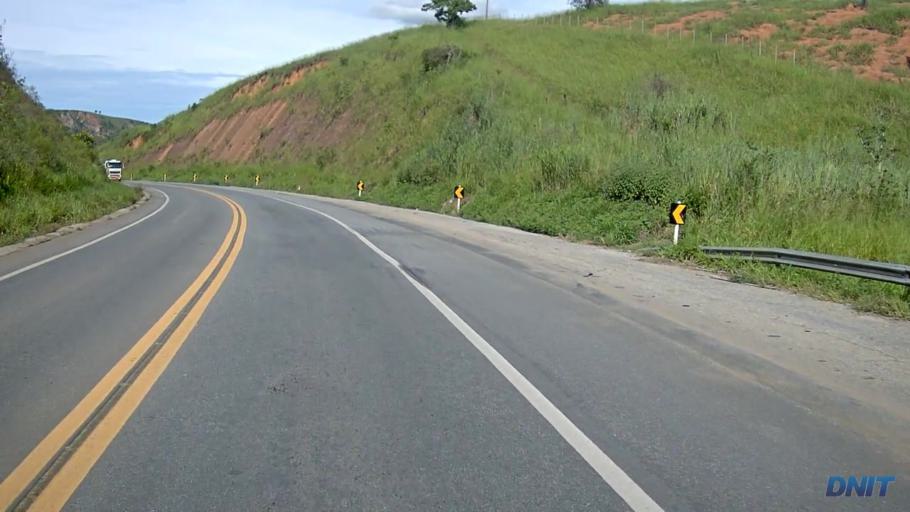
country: BR
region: Minas Gerais
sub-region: Belo Oriente
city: Belo Oriente
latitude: -19.2648
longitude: -42.3476
